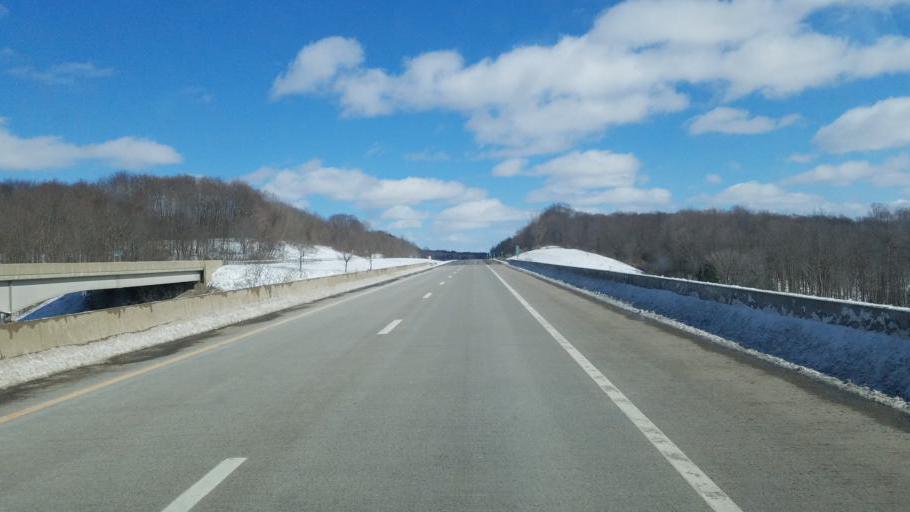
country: US
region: New York
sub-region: Chautauqua County
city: Lakewood
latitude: 42.1281
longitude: -79.3108
